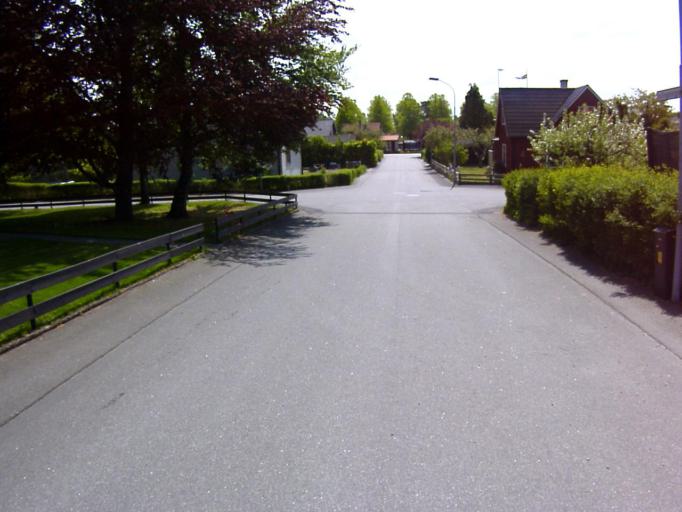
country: SE
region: Skane
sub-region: Kristianstads Kommun
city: Kristianstad
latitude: 56.0740
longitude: 14.0896
